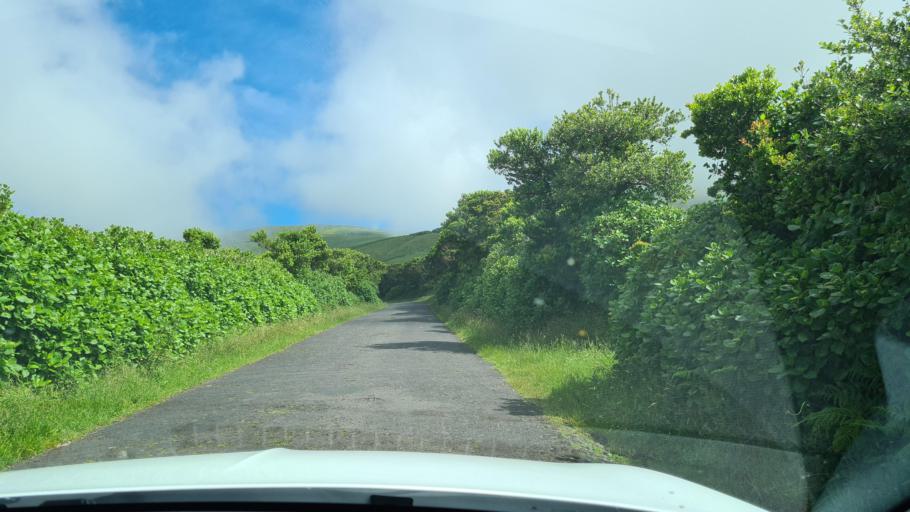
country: PT
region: Azores
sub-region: Sao Roque do Pico
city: Sao Roque do Pico
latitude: 38.6683
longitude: -28.1313
